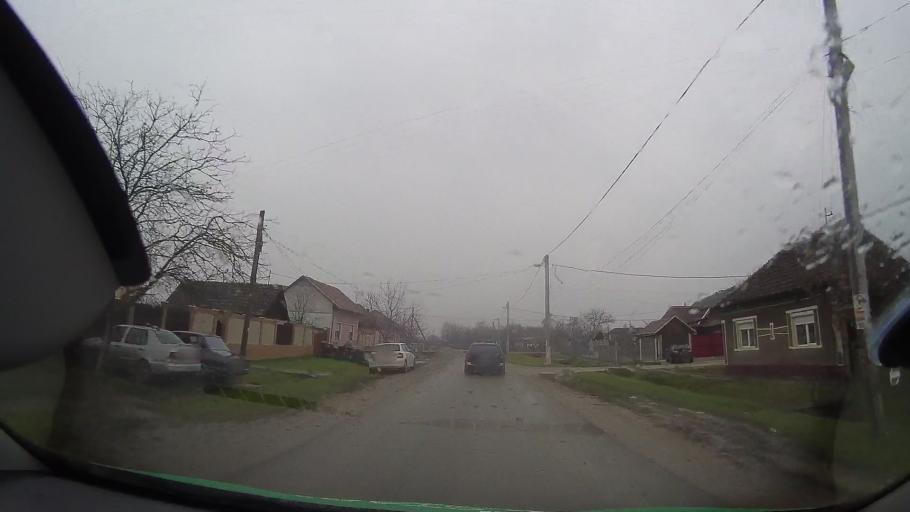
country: RO
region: Bihor
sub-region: Municipiul Salonta
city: Salonta
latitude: 46.8033
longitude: 21.6312
